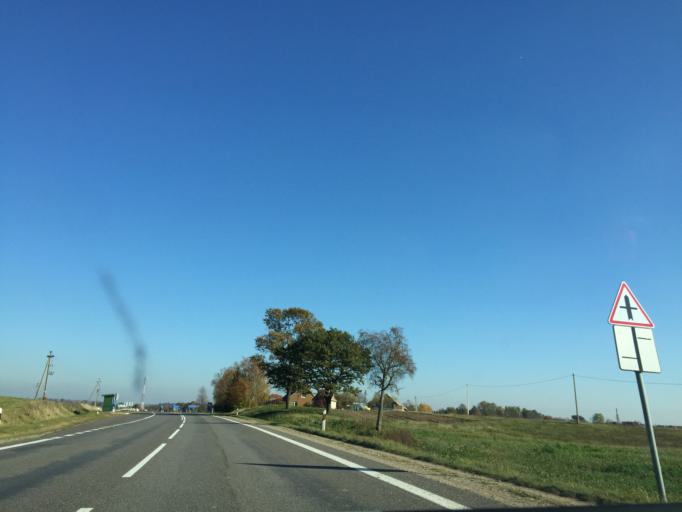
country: LT
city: Salantai
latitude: 55.9286
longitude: 21.6155
